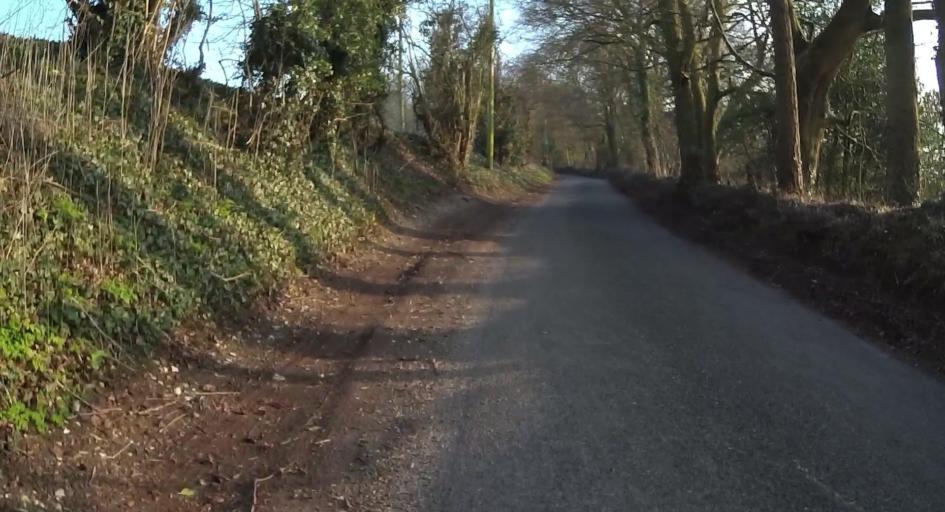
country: GB
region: England
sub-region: Hampshire
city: Alton
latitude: 51.1706
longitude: -1.0019
